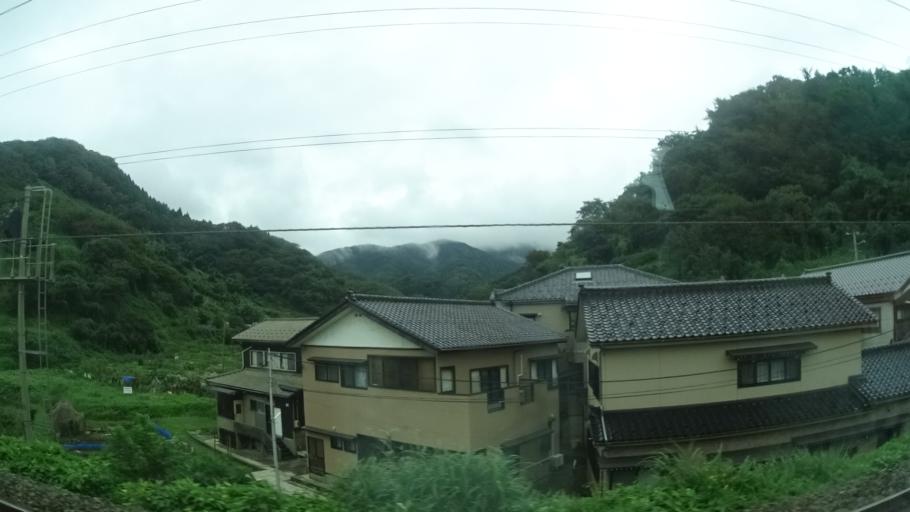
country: JP
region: Yamagata
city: Tsuruoka
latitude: 38.5921
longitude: 139.5668
